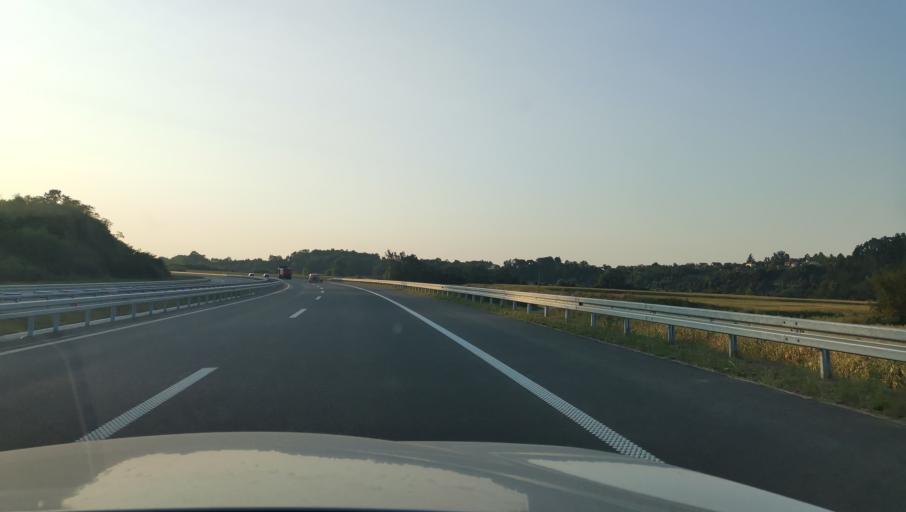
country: RS
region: Central Serbia
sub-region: Kolubarski Okrug
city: Lajkovac
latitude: 44.3403
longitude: 20.1967
